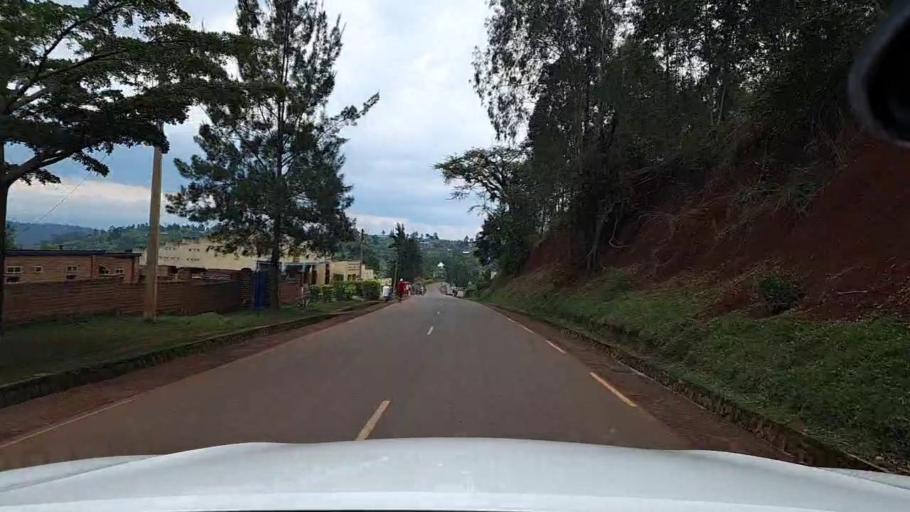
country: RW
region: Western Province
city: Cyangugu
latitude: -2.6130
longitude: 28.9398
